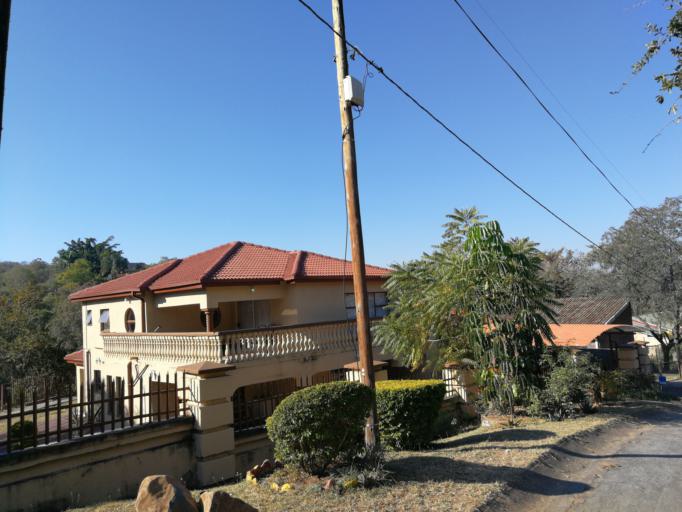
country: ZA
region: Mpumalanga
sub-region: Ehlanzeni District
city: White River
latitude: -25.0659
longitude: 31.1108
